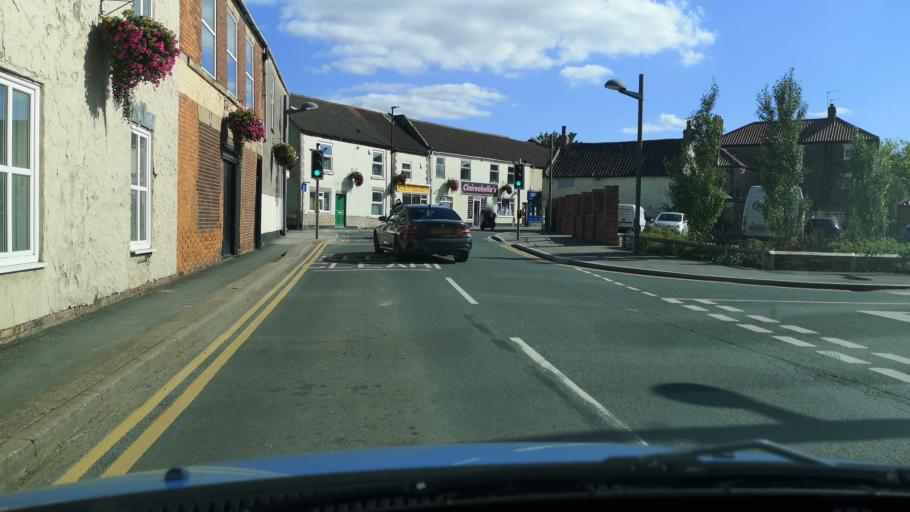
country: GB
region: England
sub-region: North Lincolnshire
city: Crowle
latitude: 53.6071
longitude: -0.8334
